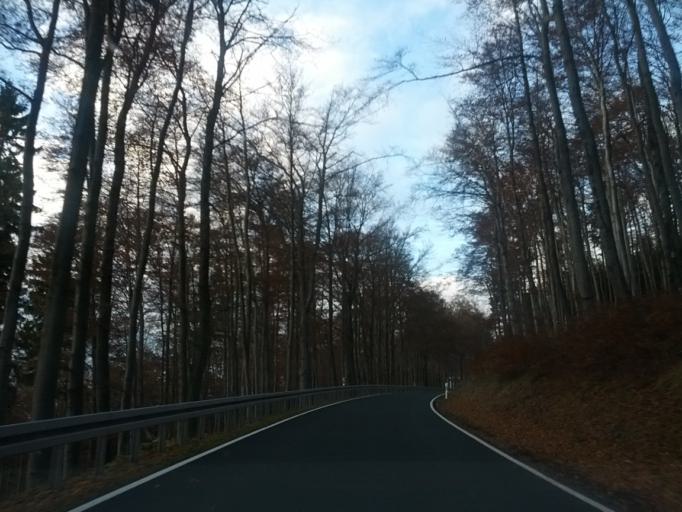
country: DE
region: Thuringia
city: Brotterode
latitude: 50.8457
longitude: 10.4062
